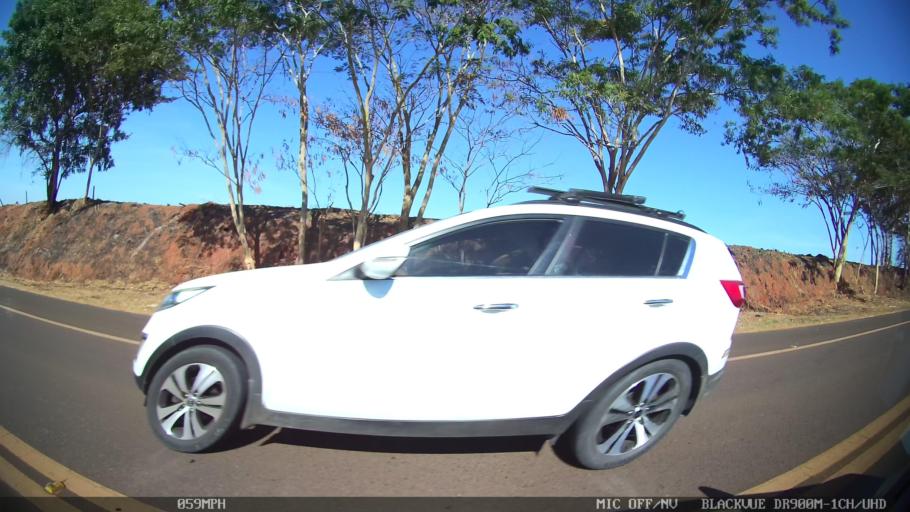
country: BR
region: Sao Paulo
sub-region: Olimpia
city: Olimpia
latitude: -20.7299
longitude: -48.8689
